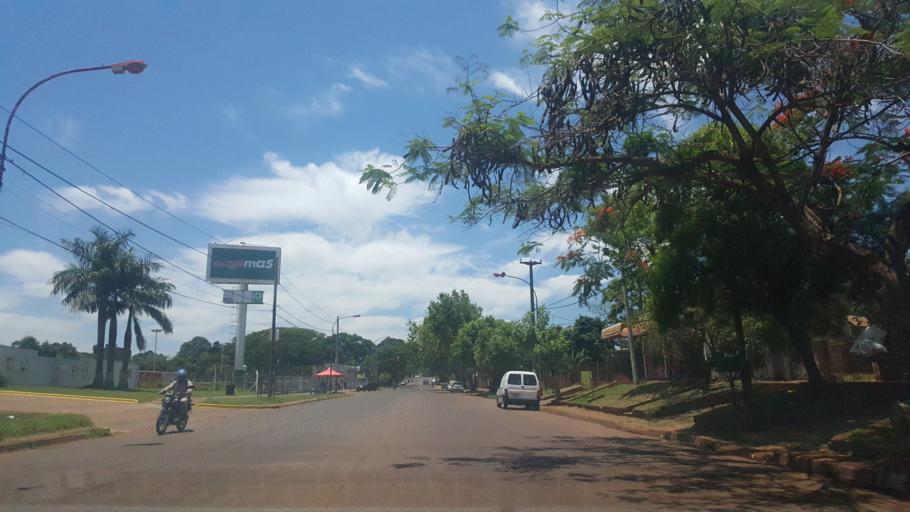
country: AR
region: Misiones
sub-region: Departamento de Capital
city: Posadas
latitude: -27.3677
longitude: -55.9278
